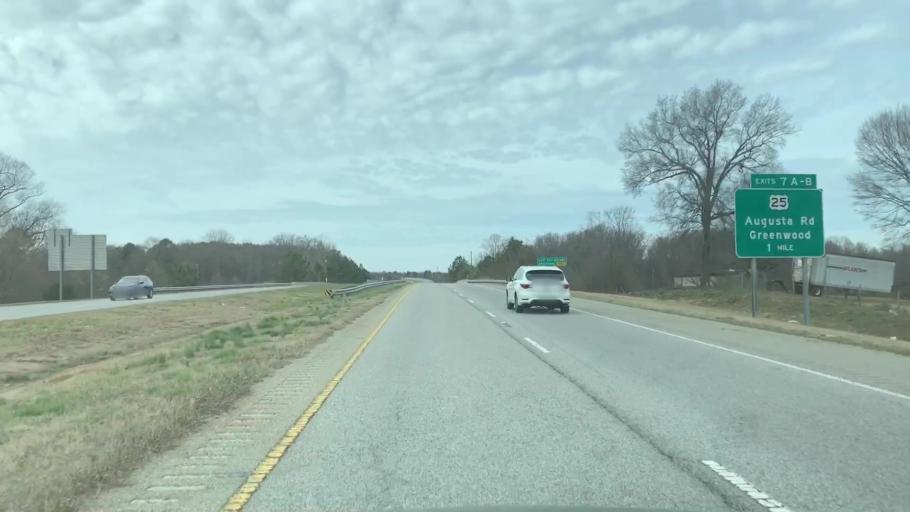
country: US
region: South Carolina
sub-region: Greenville County
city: Golden Grove
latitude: 34.7197
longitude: -82.3650
